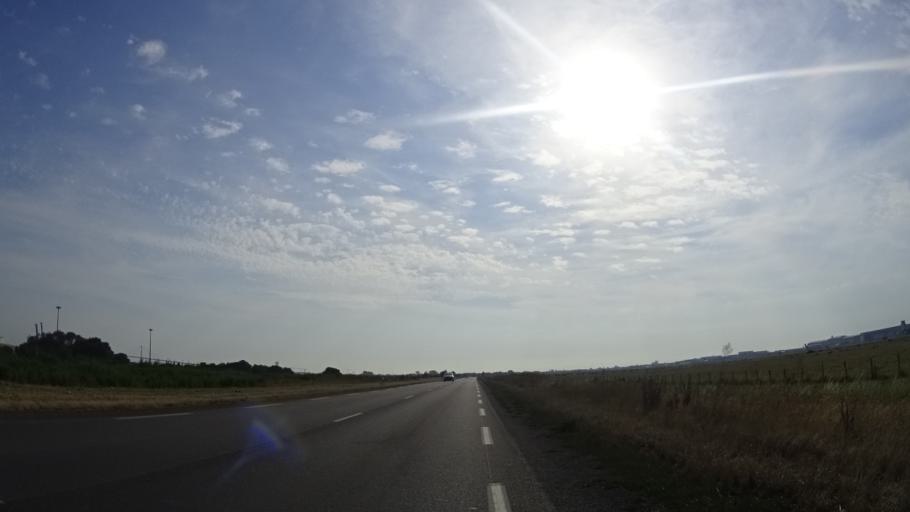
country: FR
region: Pays de la Loire
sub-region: Departement de la Loire-Atlantique
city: Montoir-de-Bretagne
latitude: 47.3086
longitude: -2.1447
